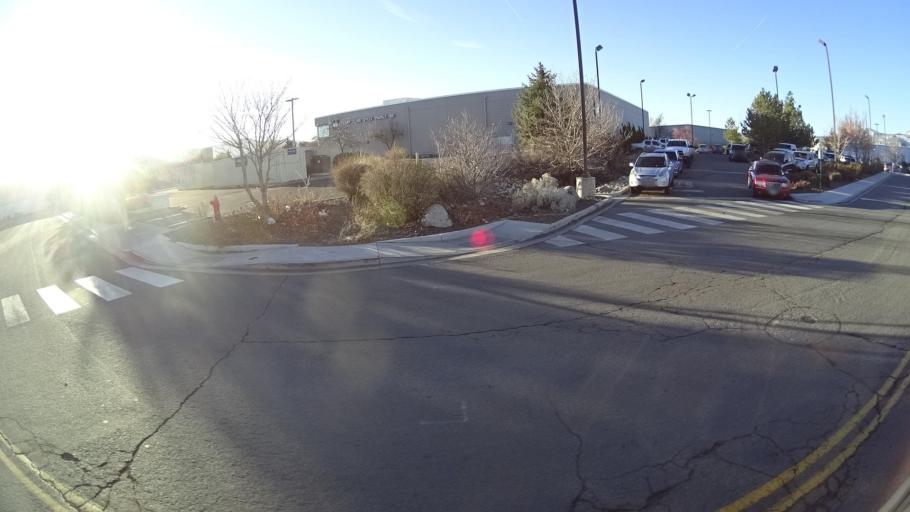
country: US
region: Nevada
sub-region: Washoe County
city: Reno
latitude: 39.5029
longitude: -119.7872
